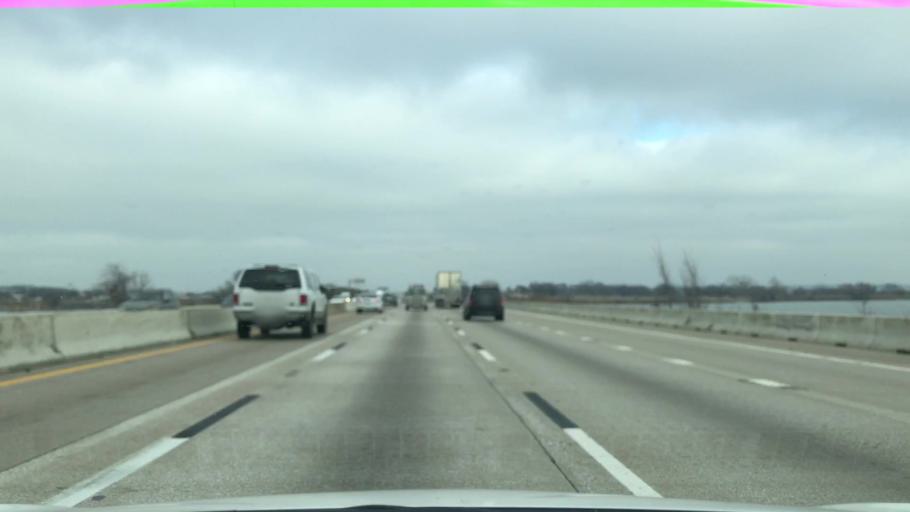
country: US
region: Texas
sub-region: Dallas County
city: Rowlett
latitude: 32.8721
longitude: -96.5280
